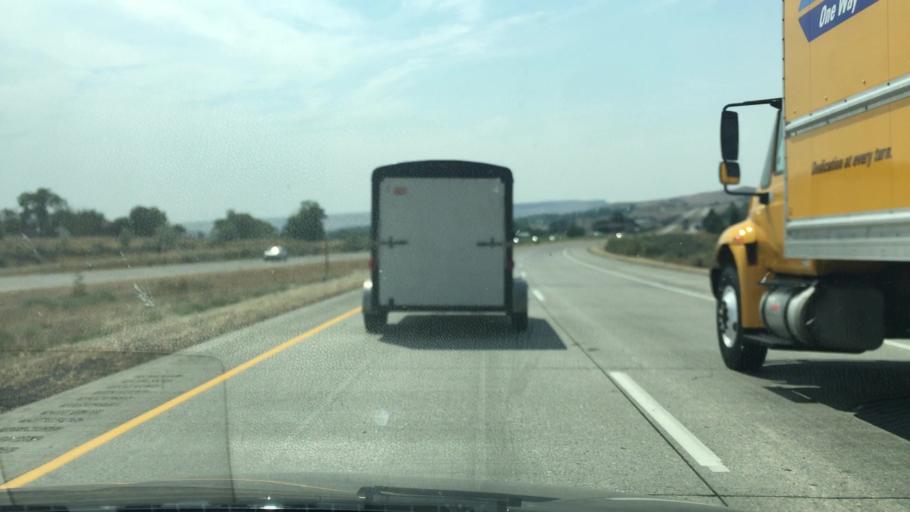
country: US
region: Idaho
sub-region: Elmore County
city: Glenns Ferry
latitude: 42.9623
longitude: -115.2608
